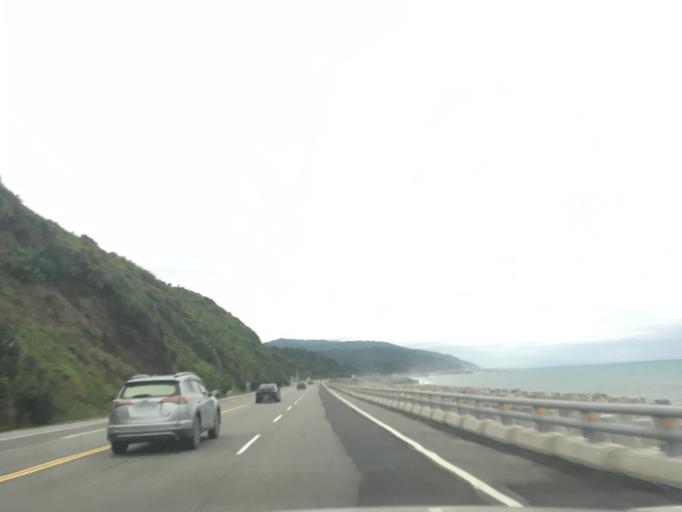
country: TW
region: Taiwan
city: Hengchun
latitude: 22.3190
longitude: 120.8916
